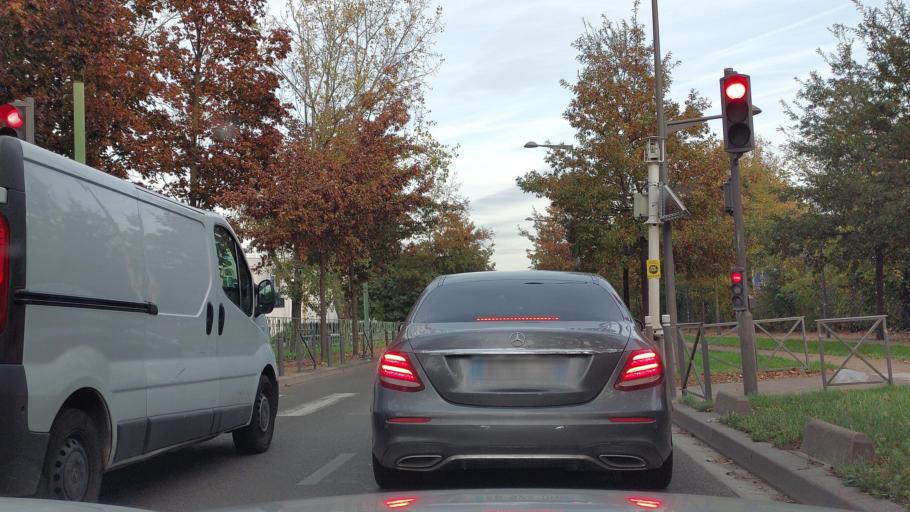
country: FR
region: Ile-de-France
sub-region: Departement de Seine-Saint-Denis
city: Aulnay-sous-Bois
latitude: 48.9519
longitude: 2.4923
